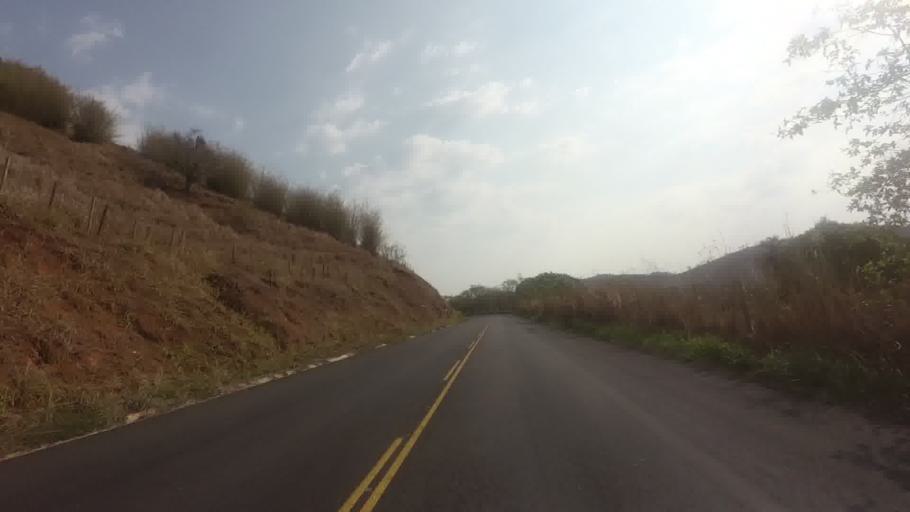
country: BR
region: Rio de Janeiro
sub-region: Itaperuna
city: Itaperuna
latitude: -21.3139
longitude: -41.8624
